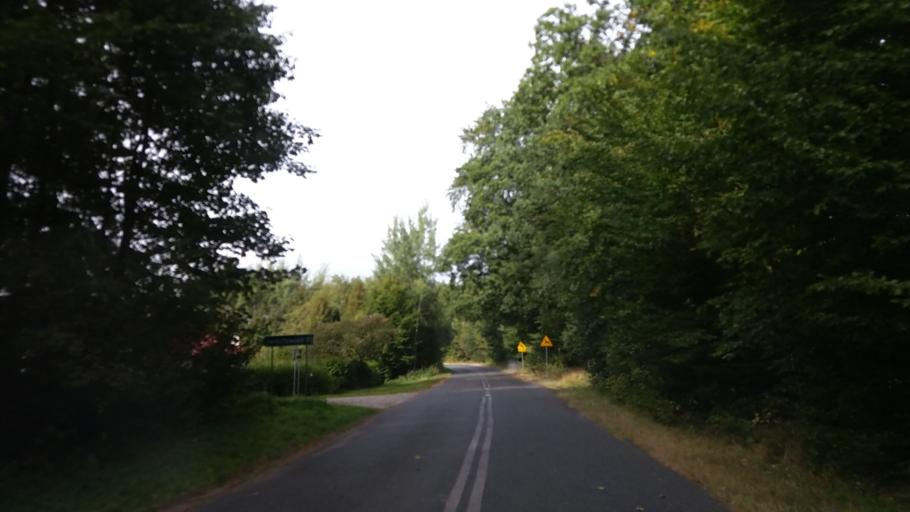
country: PL
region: West Pomeranian Voivodeship
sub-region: Powiat choszczenski
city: Krzecin
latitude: 53.0222
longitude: 15.5116
